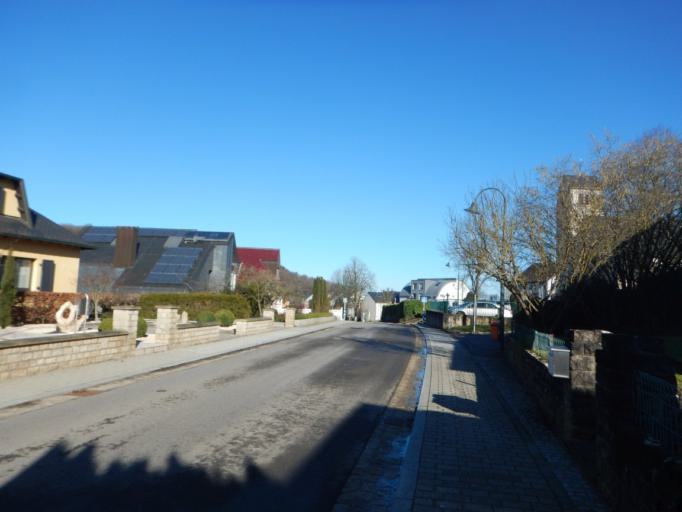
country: LU
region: Luxembourg
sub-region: Canton de Mersch
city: Lorentzweiler
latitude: 49.7036
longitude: 6.1679
